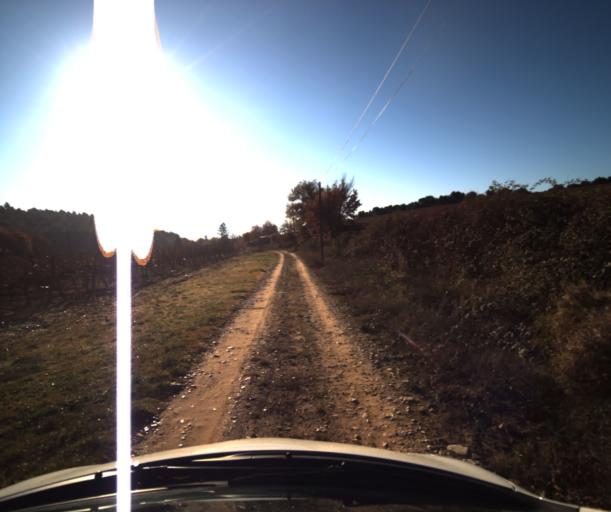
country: FR
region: Provence-Alpes-Cote d'Azur
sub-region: Departement du Vaucluse
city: Pertuis
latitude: 43.7203
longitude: 5.4937
